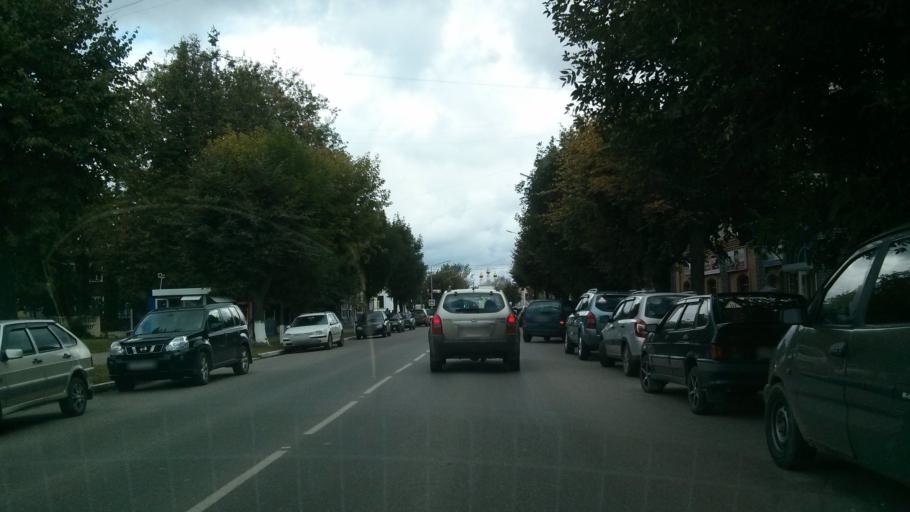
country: RU
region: Vladimir
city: Murom
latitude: 55.5748
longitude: 42.0508
